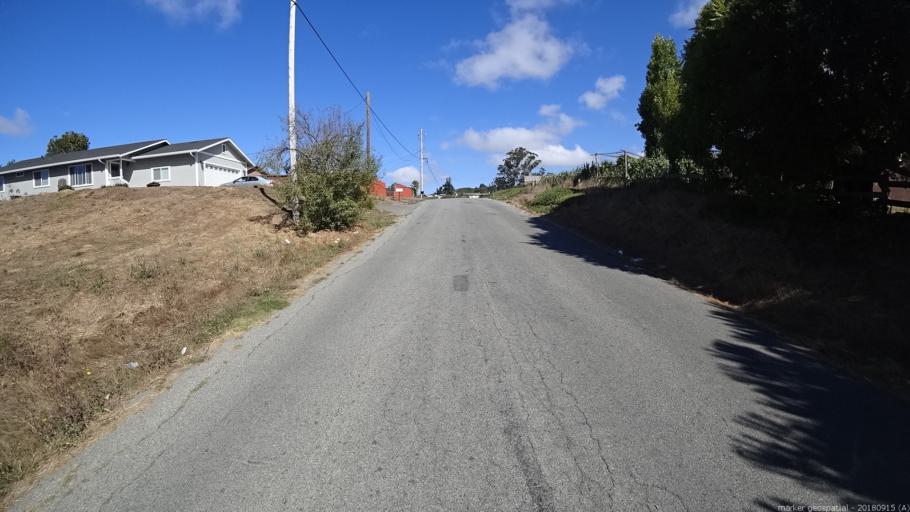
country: US
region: California
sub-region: Monterey County
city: Las Lomas
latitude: 36.8667
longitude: -121.7309
